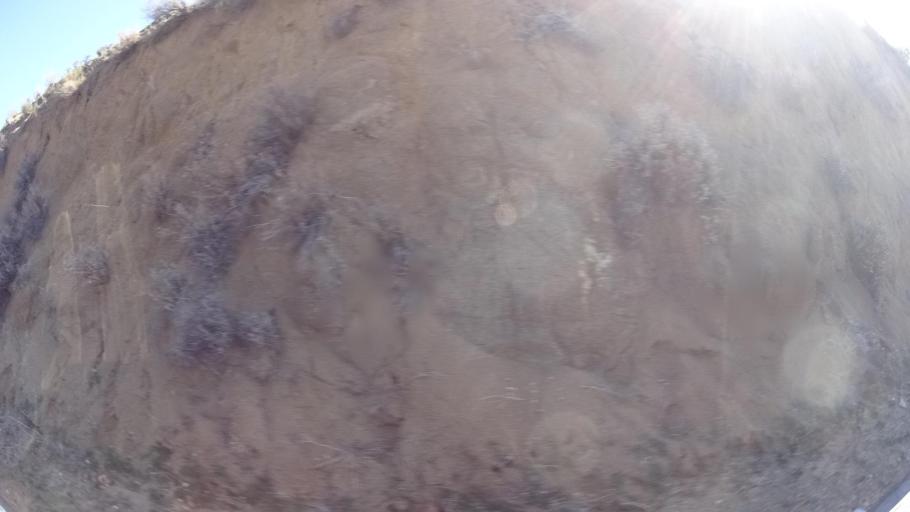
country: US
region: California
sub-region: Kern County
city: Tehachapi
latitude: 35.3454
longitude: -118.3862
